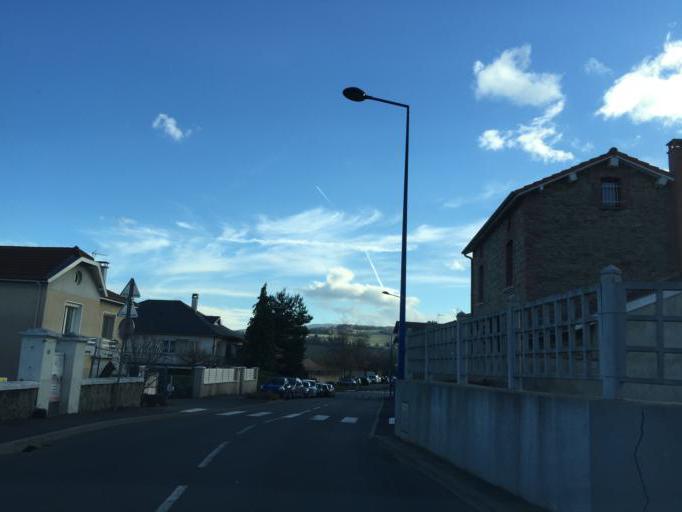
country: FR
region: Rhone-Alpes
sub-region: Departement de la Loire
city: La Talaudiere
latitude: 45.4831
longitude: 4.4377
